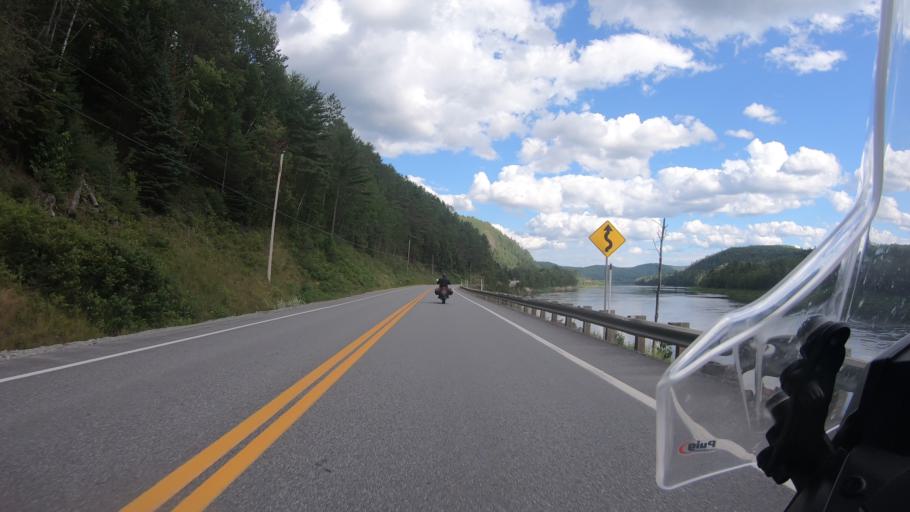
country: CA
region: Quebec
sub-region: Mauricie
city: Saint-Tite
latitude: 46.9963
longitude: -72.9198
